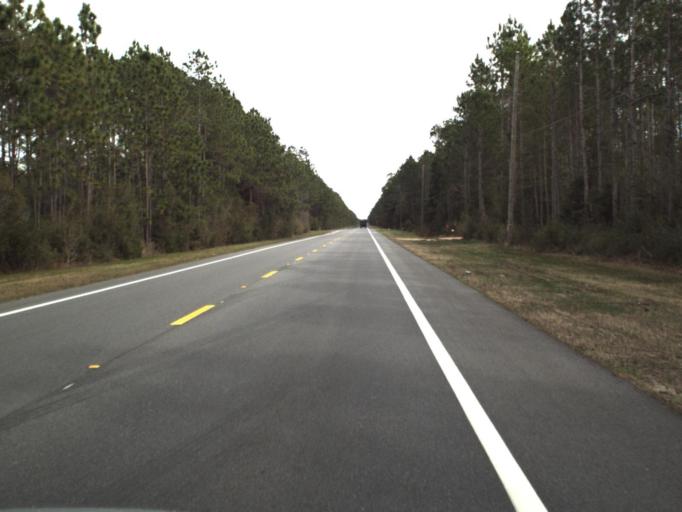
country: US
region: Florida
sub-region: Bay County
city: Callaway
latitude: 30.1527
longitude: -85.5236
